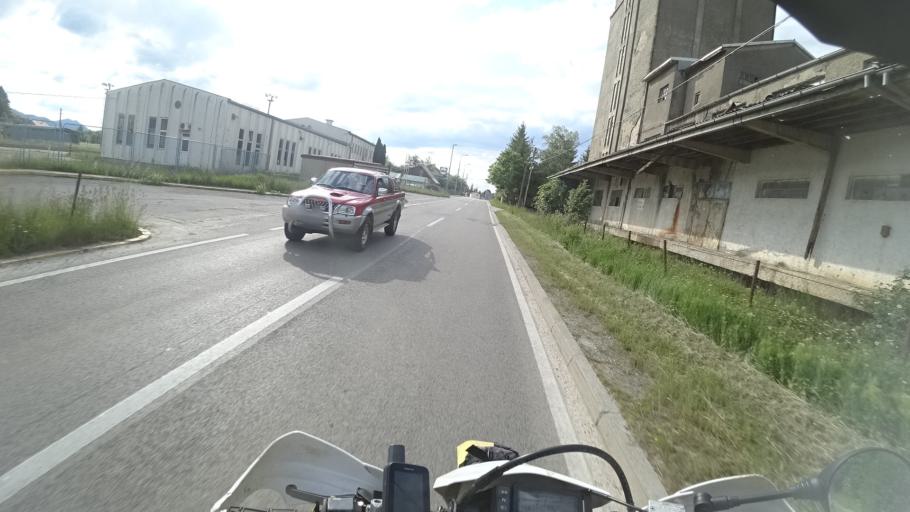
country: HR
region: Licko-Senjska
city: Gospic
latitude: 44.5335
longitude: 15.3976
